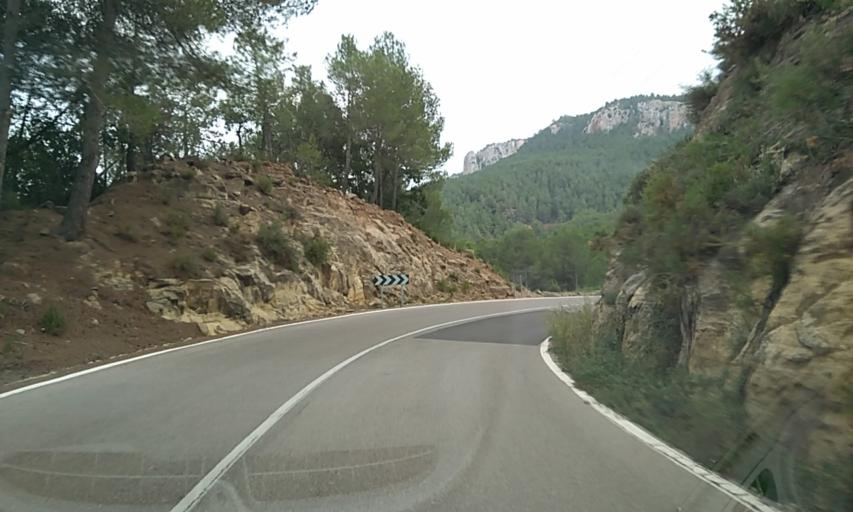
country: ES
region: Valencia
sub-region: Provincia de Castello
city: Puebla de Arenoso
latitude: 40.0894
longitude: -0.5684
